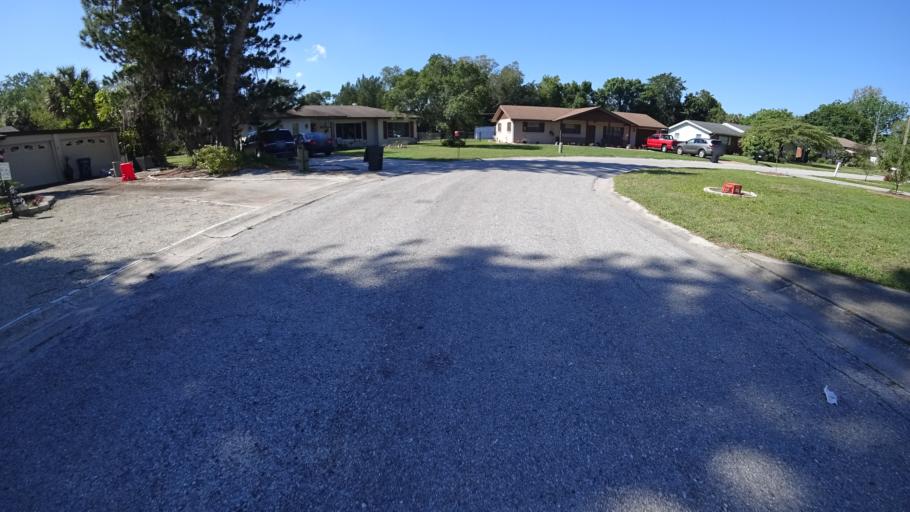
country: US
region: Florida
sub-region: Manatee County
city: West Bradenton
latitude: 27.4743
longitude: -82.6092
